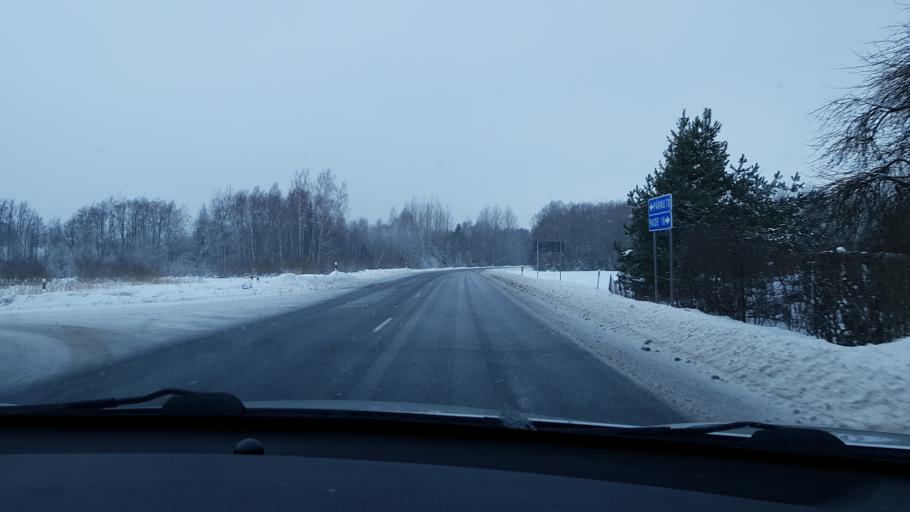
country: EE
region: Jaervamaa
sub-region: Tueri vald
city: Sarevere
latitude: 58.7673
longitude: 25.4169
